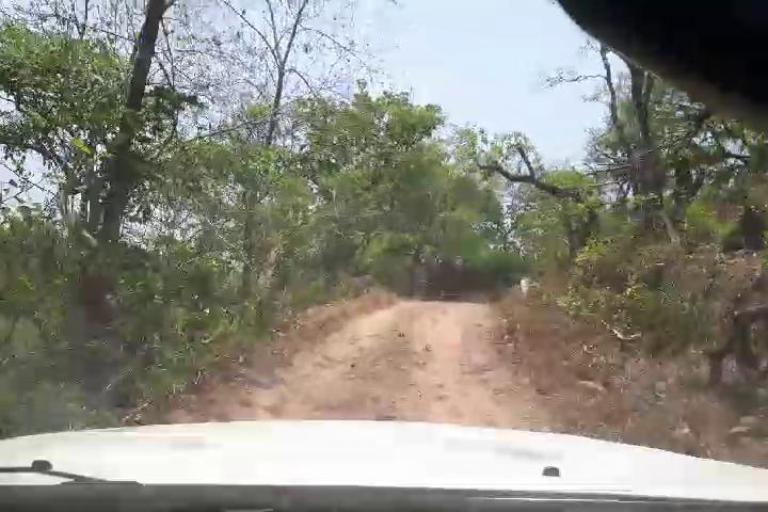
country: SL
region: Northern Province
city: Alikalia
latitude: 9.0781
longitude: -11.4722
